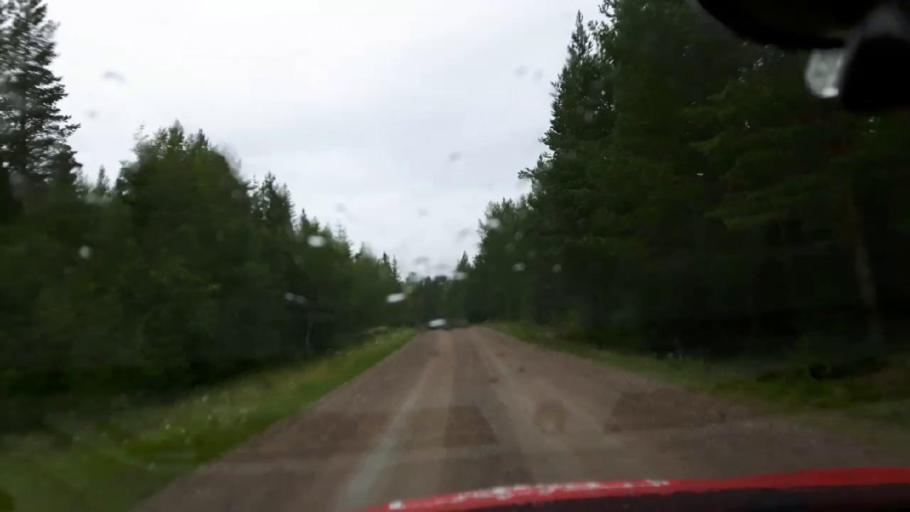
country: SE
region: Jaemtland
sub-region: OEstersunds Kommun
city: Brunflo
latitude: 62.8085
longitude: 14.8938
